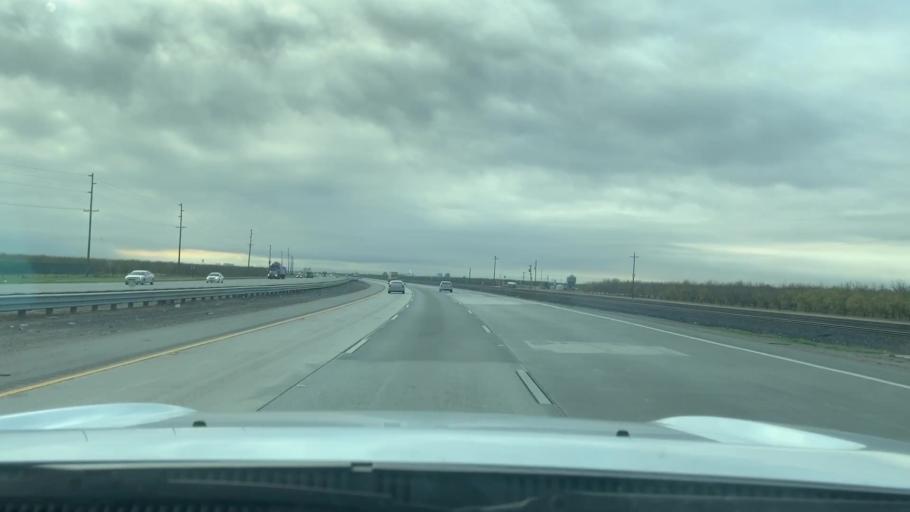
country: US
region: California
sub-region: Kern County
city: Shafter
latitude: 35.5256
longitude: -119.1885
